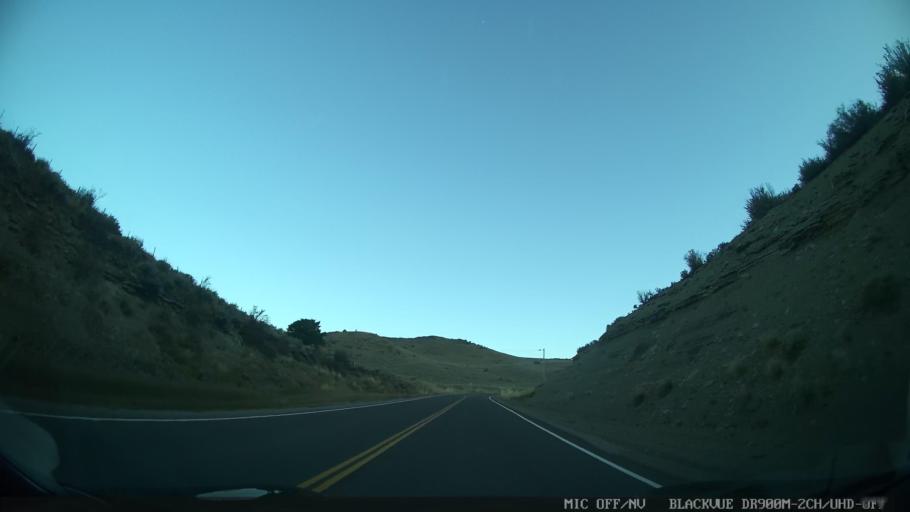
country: US
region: Colorado
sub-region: Eagle County
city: Edwards
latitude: 39.8064
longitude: -106.6777
